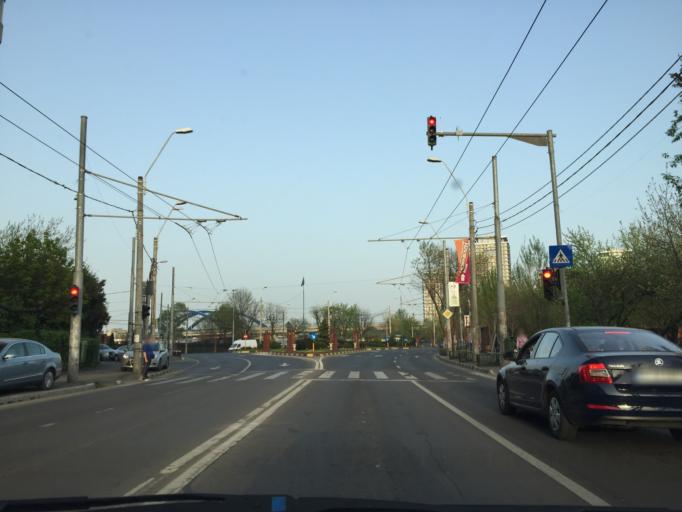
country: RO
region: Bucuresti
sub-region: Municipiul Bucuresti
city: Bucharest
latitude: 44.4084
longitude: 26.1177
